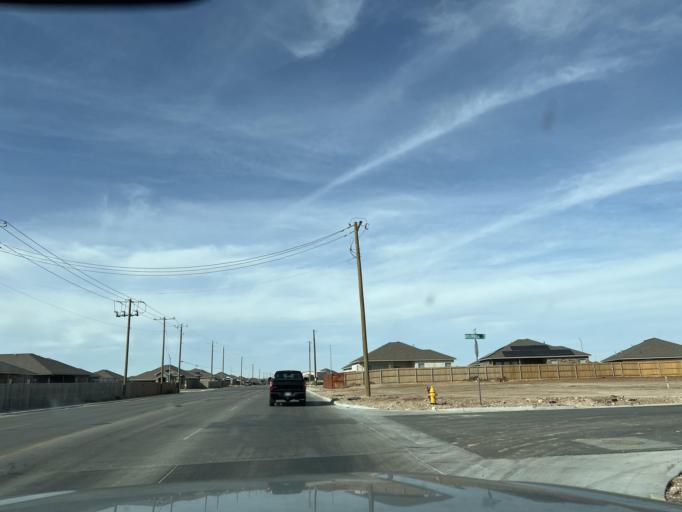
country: US
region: Texas
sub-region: Ector County
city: Gardendale
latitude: 31.9406
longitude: -102.3841
